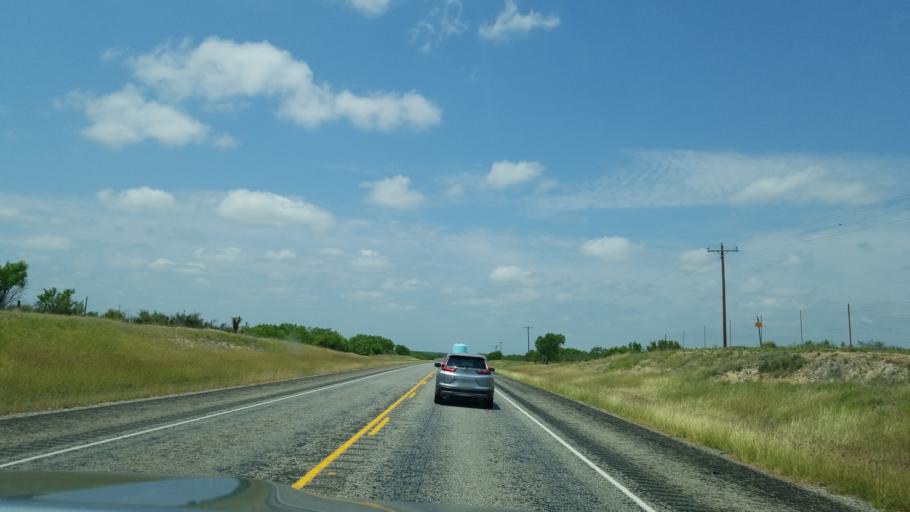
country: US
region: Texas
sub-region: Zavala County
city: La Pryor
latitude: 28.9335
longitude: -99.7466
